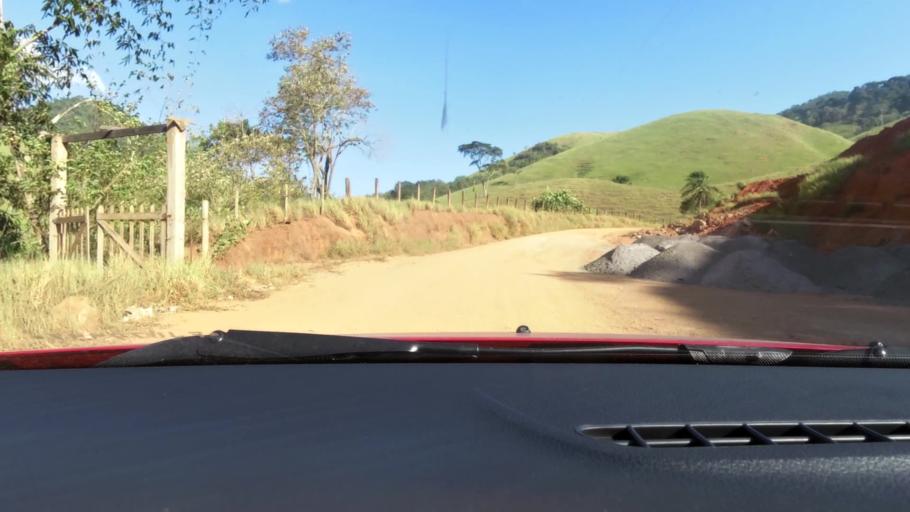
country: BR
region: Espirito Santo
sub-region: Guarapari
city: Guarapari
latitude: -20.5290
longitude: -40.5642
